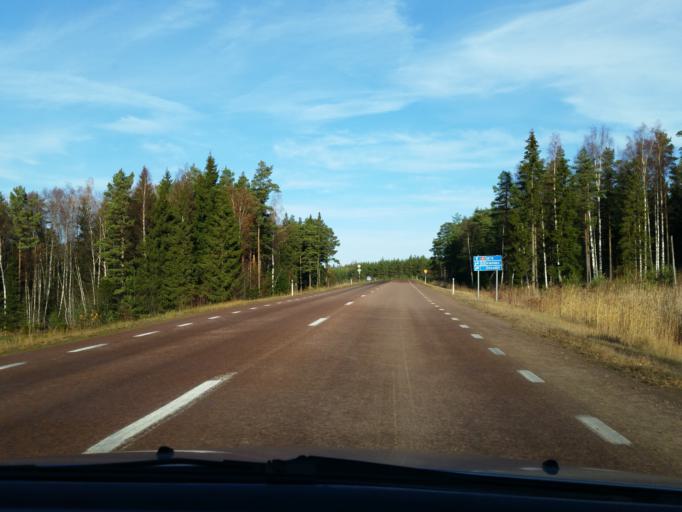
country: AX
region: Alands landsbygd
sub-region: Finstroem
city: Finstroem
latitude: 60.3016
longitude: 19.9525
